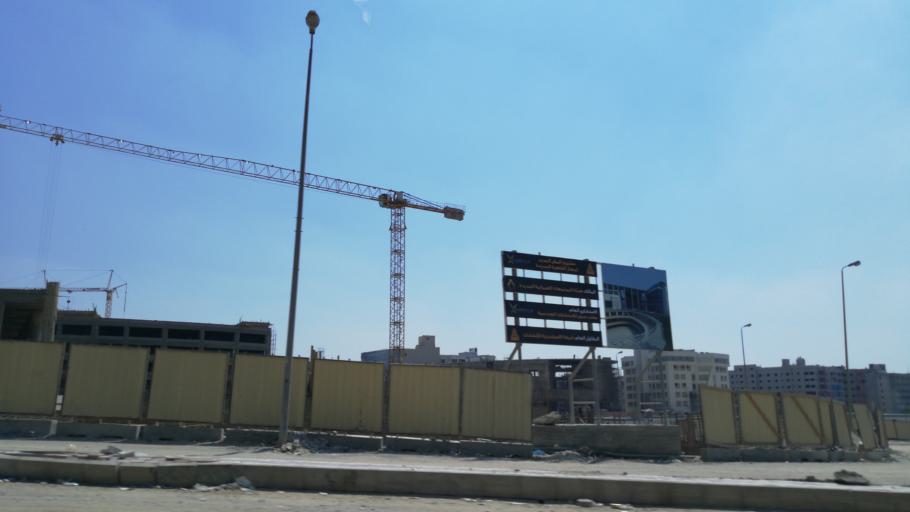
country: EG
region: Muhafazat al Qalyubiyah
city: Al Khankah
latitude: 30.0293
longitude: 31.4688
